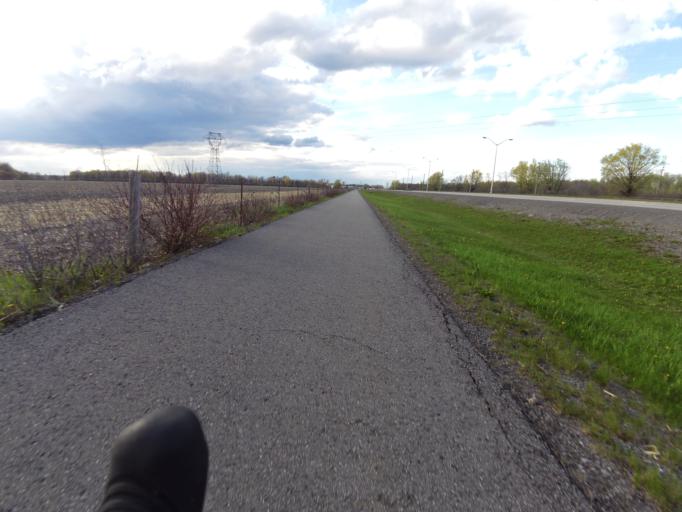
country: CA
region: Ontario
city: Ottawa
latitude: 45.3090
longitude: -75.6836
